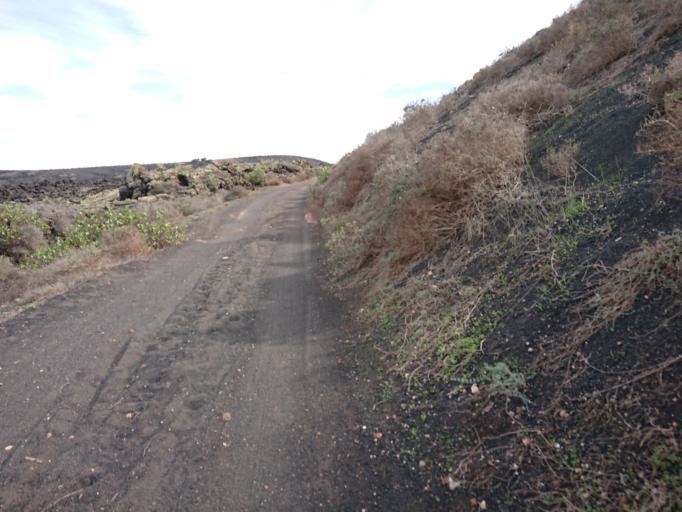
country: ES
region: Canary Islands
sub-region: Provincia de Las Palmas
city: Tinajo
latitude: 29.0203
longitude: -13.6772
